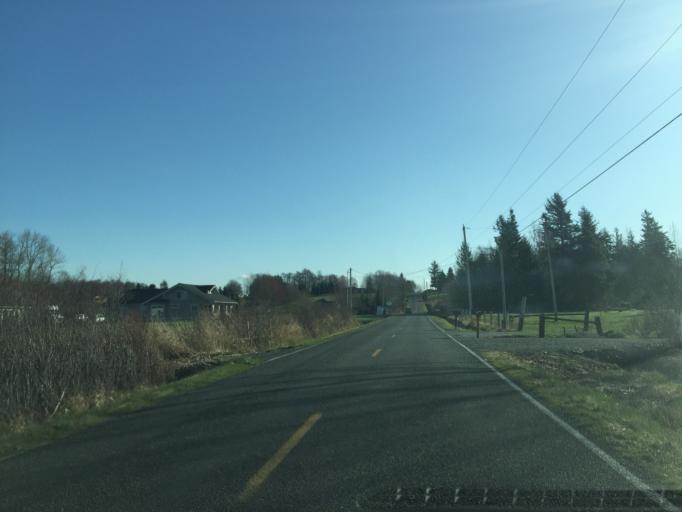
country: US
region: Washington
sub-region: Whatcom County
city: Marietta-Alderwood
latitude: 48.8189
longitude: -122.5168
